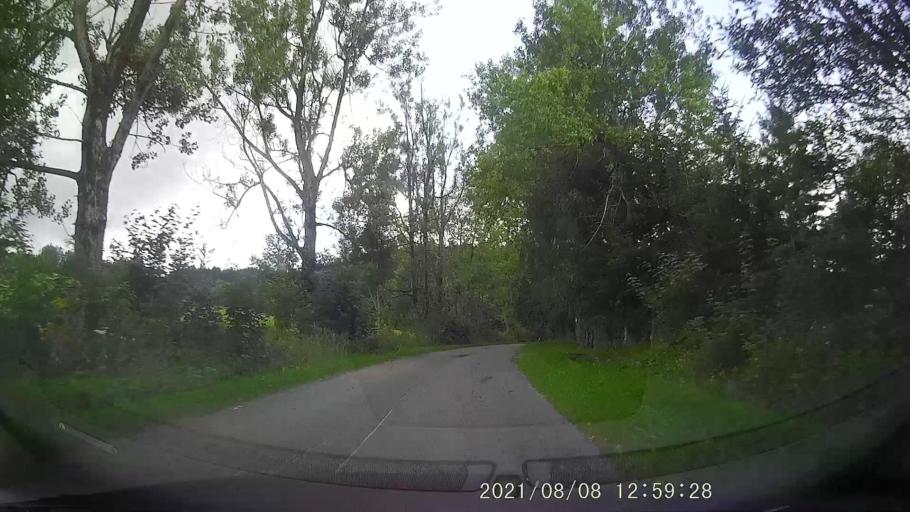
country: PL
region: Lower Silesian Voivodeship
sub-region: Powiat klodzki
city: Duszniki-Zdroj
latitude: 50.4105
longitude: 16.3487
